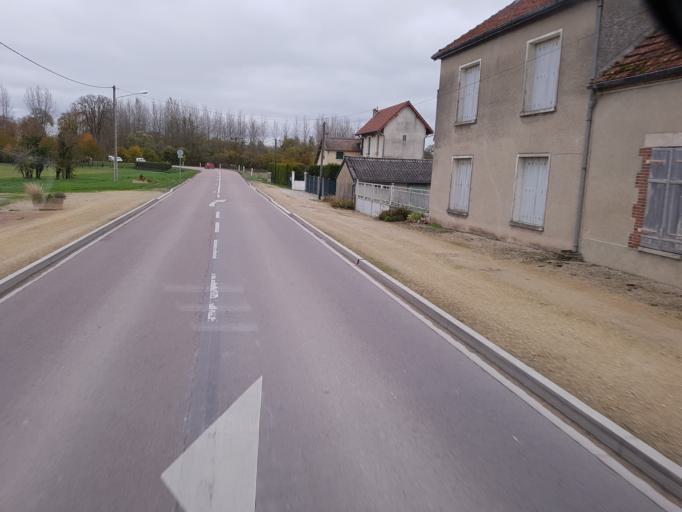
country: FR
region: Champagne-Ardenne
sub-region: Departement de l'Aube
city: Mery-sur-Seine
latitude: 48.4880
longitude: 3.8847
